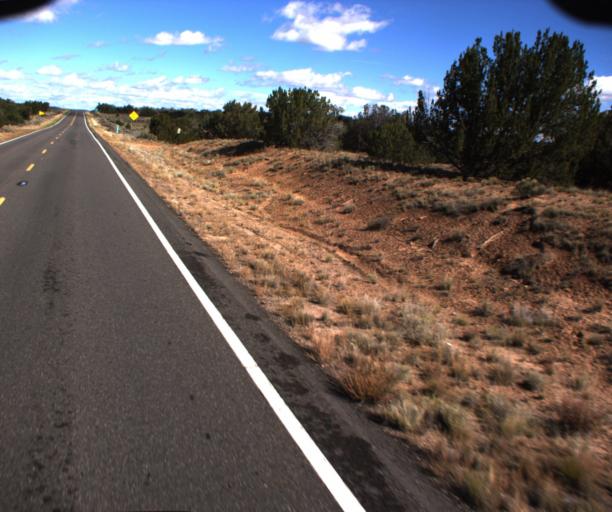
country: US
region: Arizona
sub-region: Apache County
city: Houck
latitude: 34.8922
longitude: -109.2380
